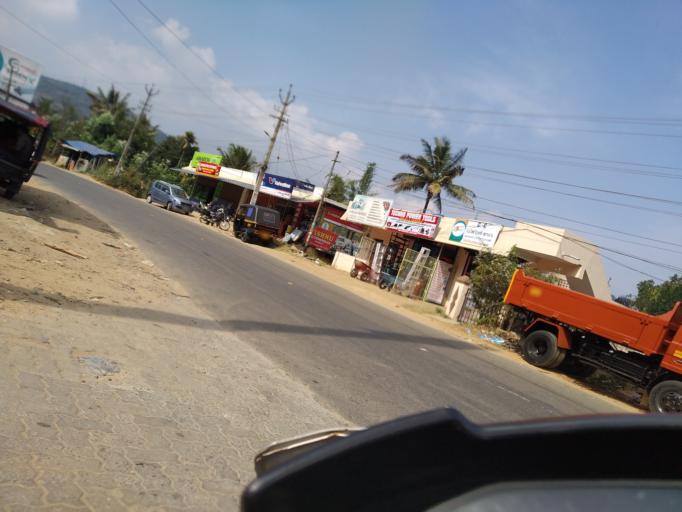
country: IN
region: Tamil Nadu
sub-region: Theni
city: Gudalur
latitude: 9.6129
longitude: 77.1566
